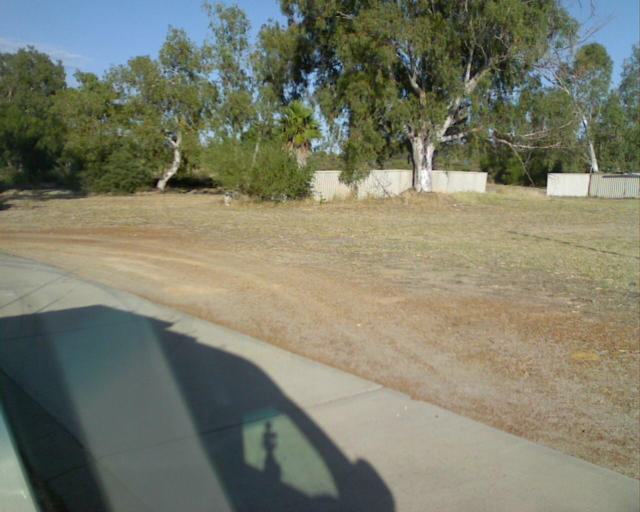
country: AU
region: Western Australia
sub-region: Dandaragan
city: Jurien Bay
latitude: -29.8219
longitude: 115.2698
